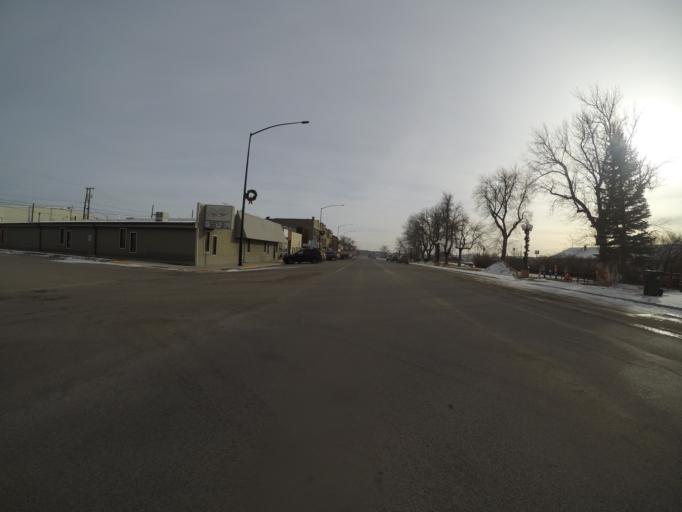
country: US
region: Montana
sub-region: Stillwater County
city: Columbus
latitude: 45.6372
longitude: -109.2539
